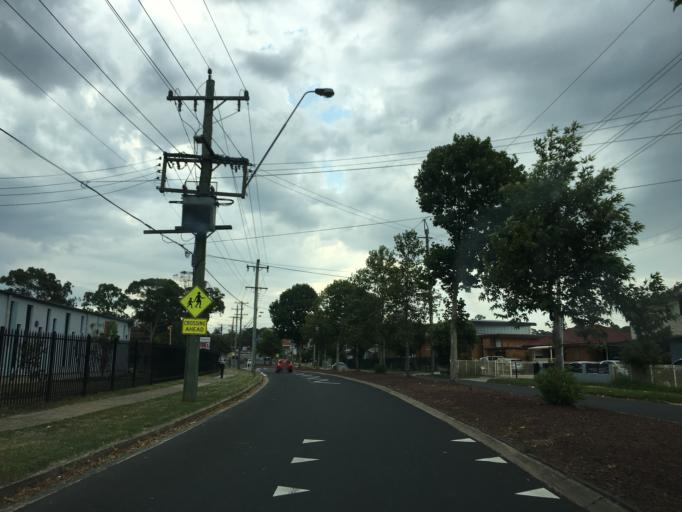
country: AU
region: New South Wales
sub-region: Liverpool
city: Miller
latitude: -33.9206
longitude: 150.8877
